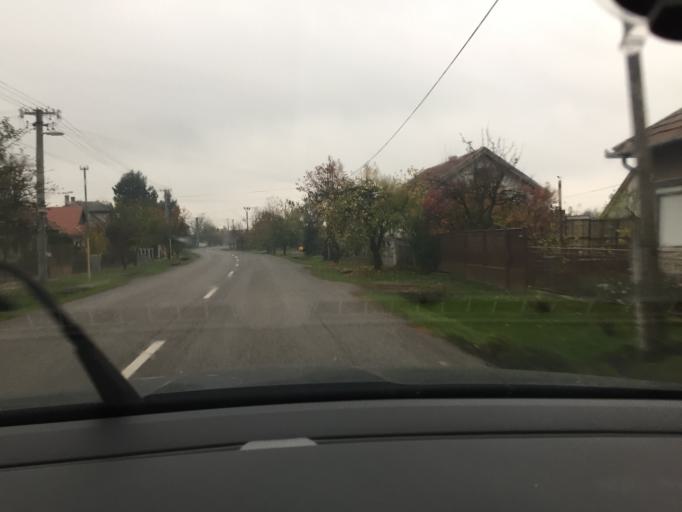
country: SK
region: Banskobystricky
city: Dudince
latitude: 48.0611
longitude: 18.8118
